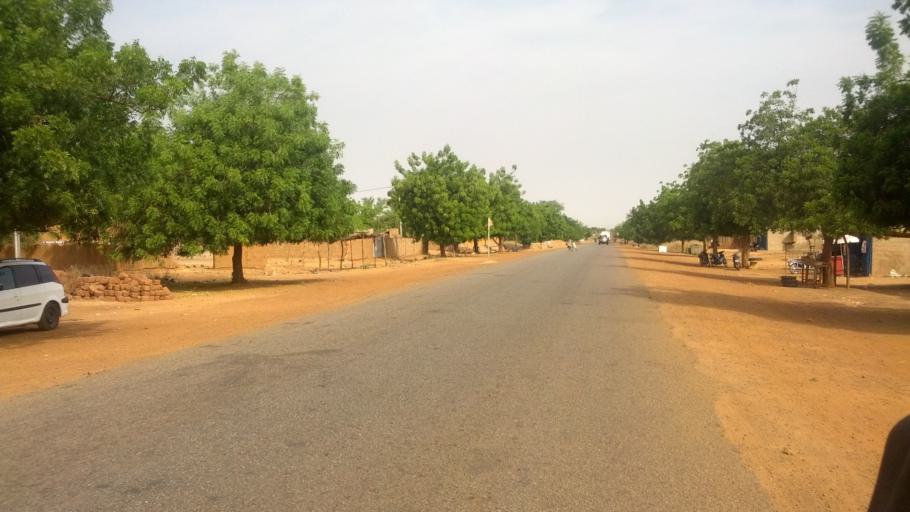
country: BF
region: Centre-Nord
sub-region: Province du Sanmatenga
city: Kaya
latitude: 12.9122
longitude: -1.0781
